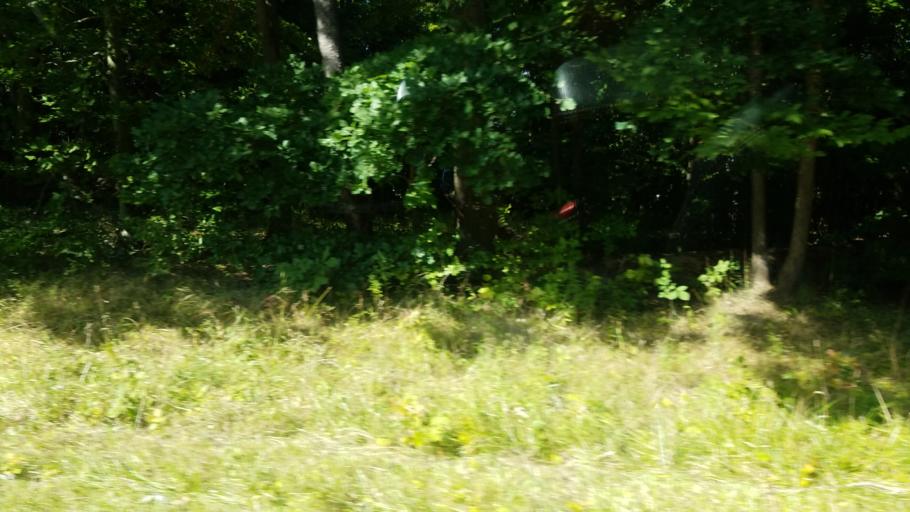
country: US
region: Ohio
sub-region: Mahoning County
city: Canfield
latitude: 41.0425
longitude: -80.7280
